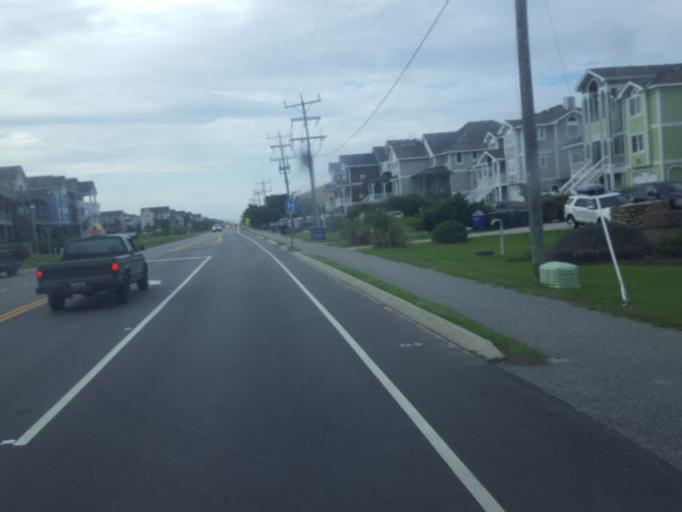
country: US
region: North Carolina
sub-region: Dare County
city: Nags Head
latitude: 35.9384
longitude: -75.6135
